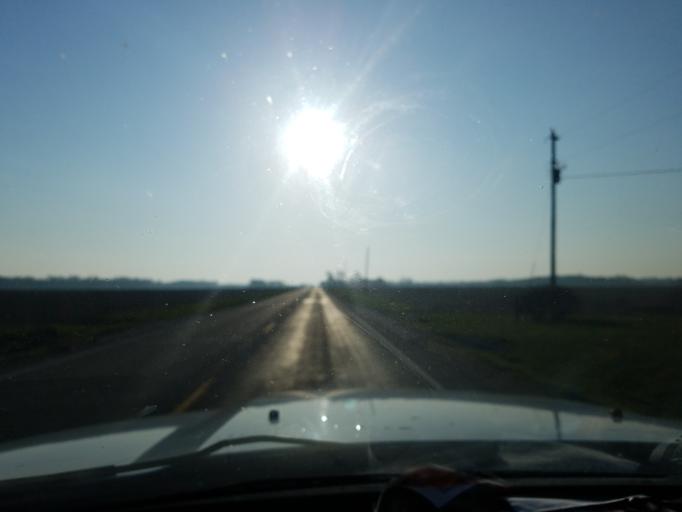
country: US
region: Indiana
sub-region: Vigo County
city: Seelyville
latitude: 39.3889
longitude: -87.1977
